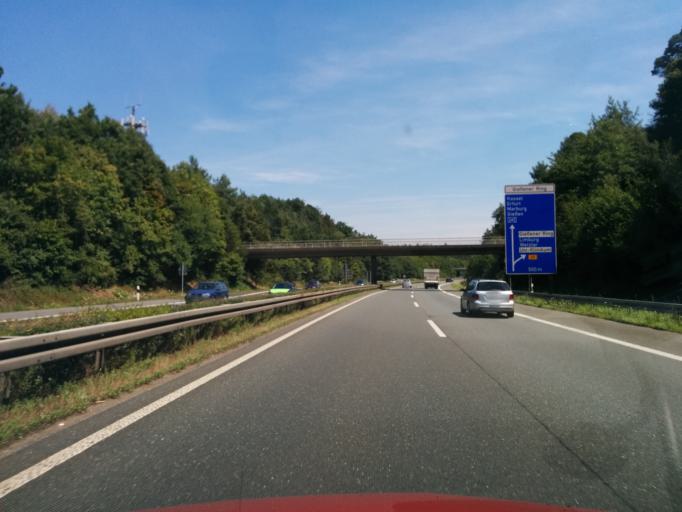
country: DE
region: Hesse
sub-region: Regierungsbezirk Giessen
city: Giessen
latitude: 50.5523
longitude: 8.6596
